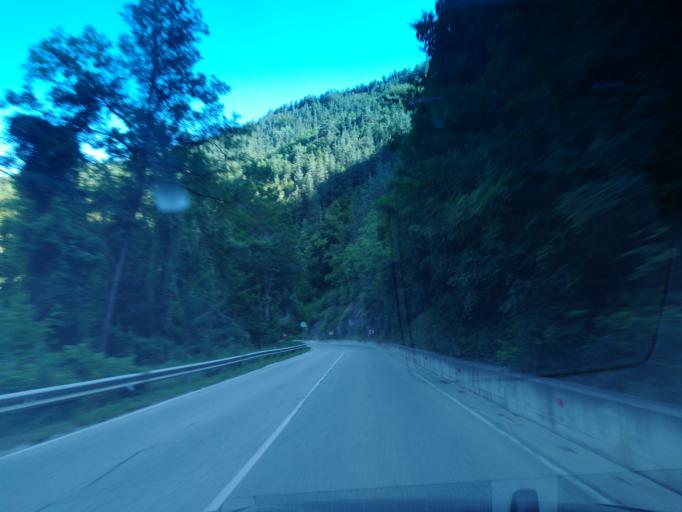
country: BG
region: Smolyan
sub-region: Obshtina Chepelare
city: Chepelare
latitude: 41.8228
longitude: 24.6922
